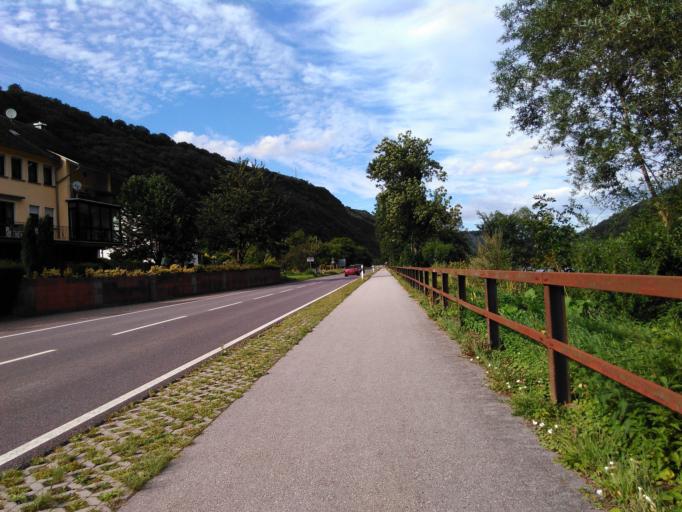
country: DE
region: Rheinland-Pfalz
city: Moselkern
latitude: 50.1954
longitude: 7.3728
